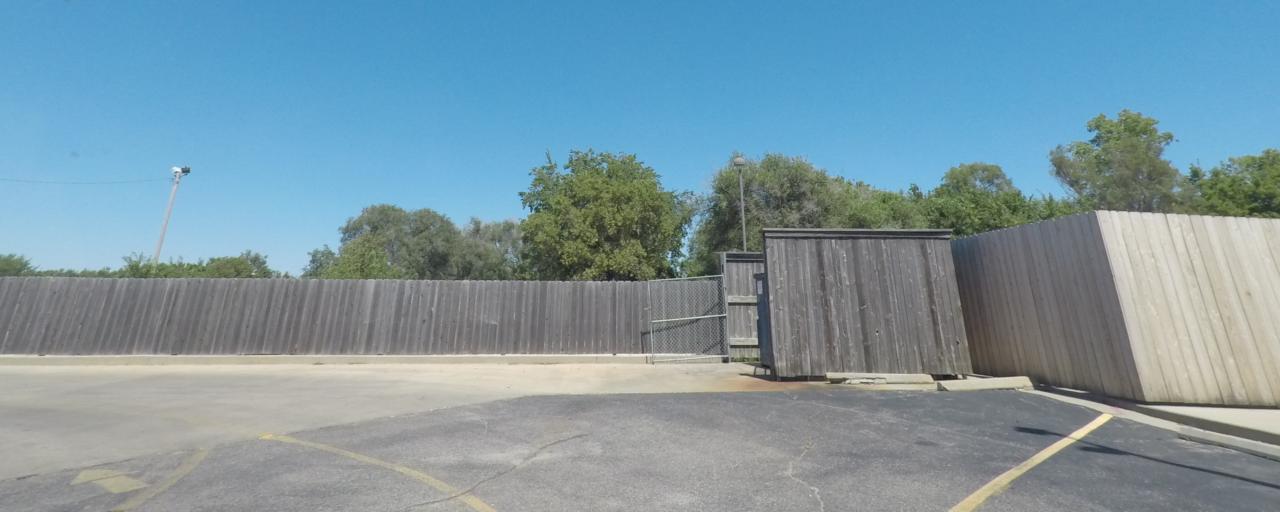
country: US
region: Kansas
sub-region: Sedgwick County
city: Wichita
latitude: 37.6520
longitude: -97.3558
